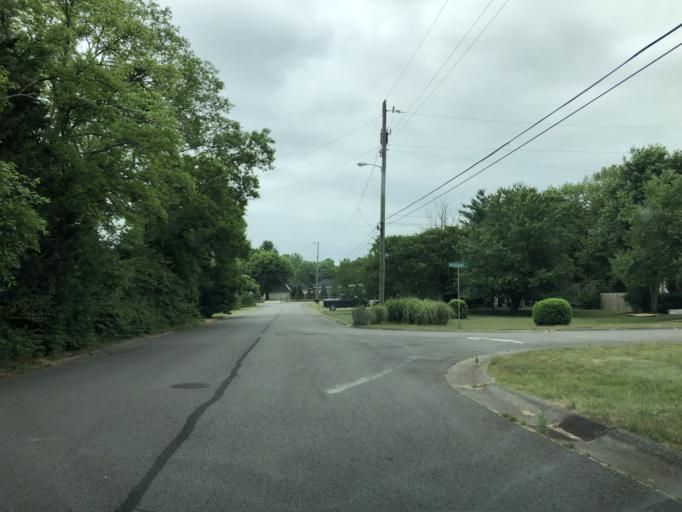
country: US
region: Tennessee
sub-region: Davidson County
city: Goodlettsville
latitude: 36.2910
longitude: -86.7459
